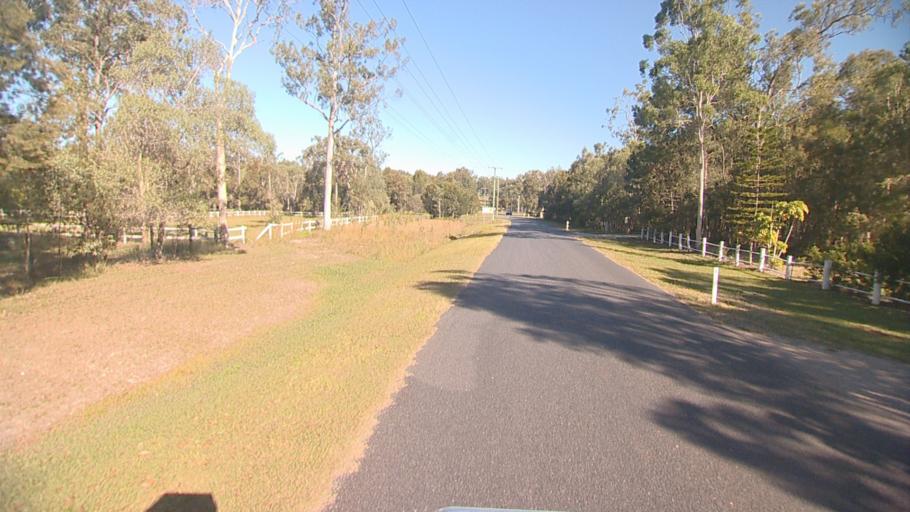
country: AU
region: Queensland
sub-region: Logan
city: Chambers Flat
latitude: -27.7325
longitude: 153.0719
